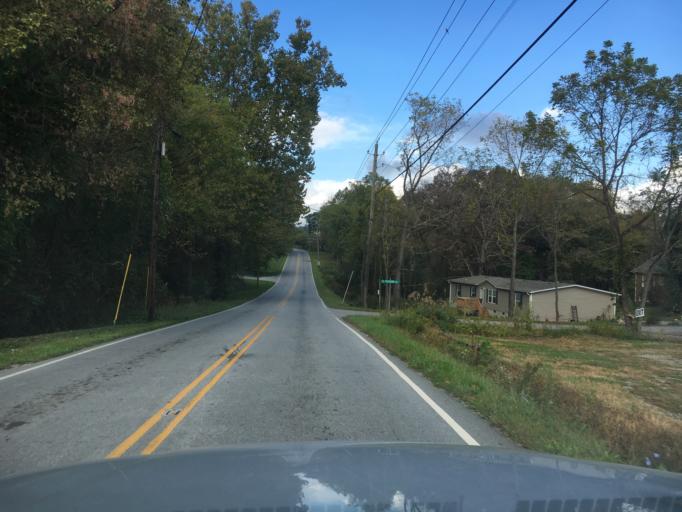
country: US
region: North Carolina
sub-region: Henderson County
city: Fletcher
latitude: 35.4309
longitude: -82.5020
